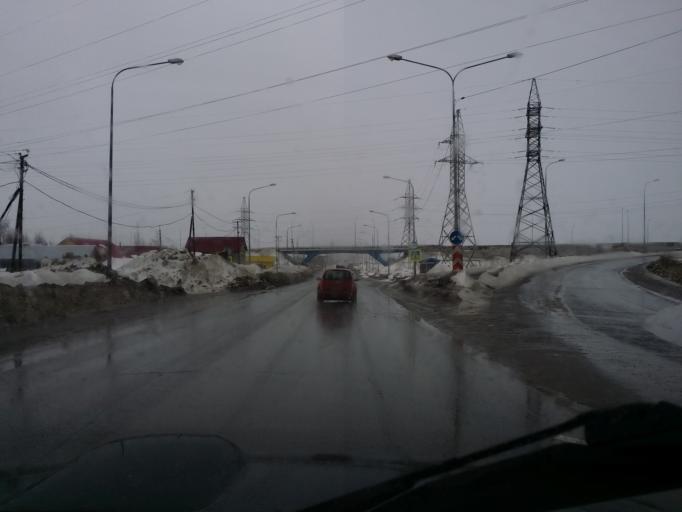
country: RU
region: Khanty-Mansiyskiy Avtonomnyy Okrug
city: Nizhnevartovsk
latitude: 60.9483
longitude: 76.6672
